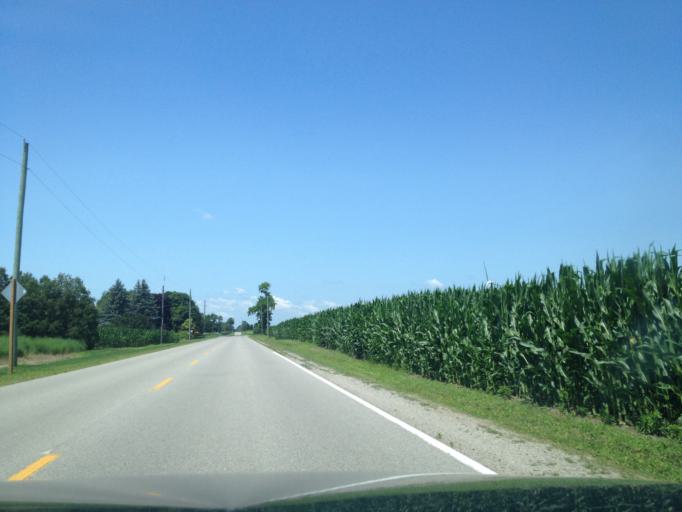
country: CA
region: Ontario
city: Aylmer
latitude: 42.6070
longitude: -80.6779
